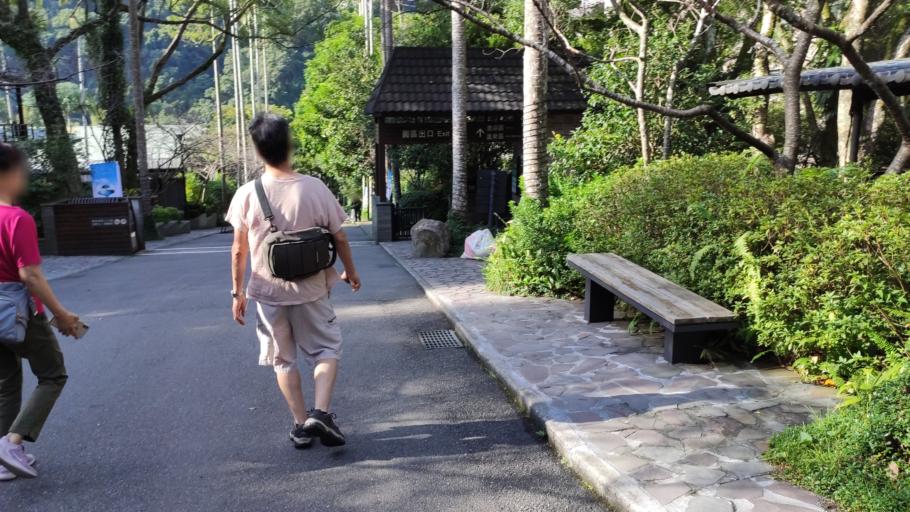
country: TW
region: Taiwan
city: Daxi
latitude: 24.8718
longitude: 121.4078
